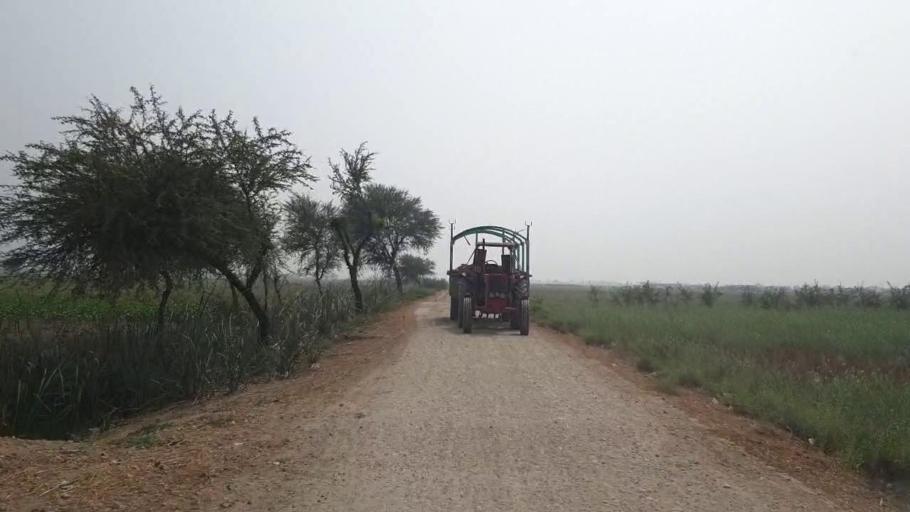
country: PK
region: Sindh
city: Kario
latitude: 24.6529
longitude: 68.5957
